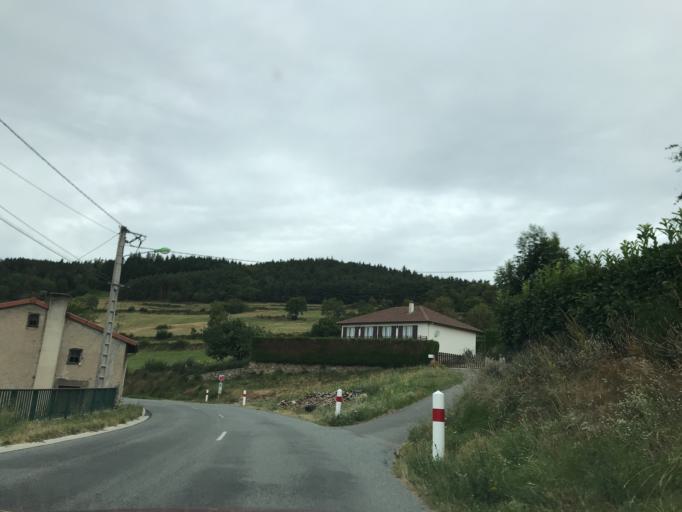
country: FR
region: Rhone-Alpes
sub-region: Departement de la Loire
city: Sail-sous-Couzan
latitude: 45.6967
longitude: 3.9177
